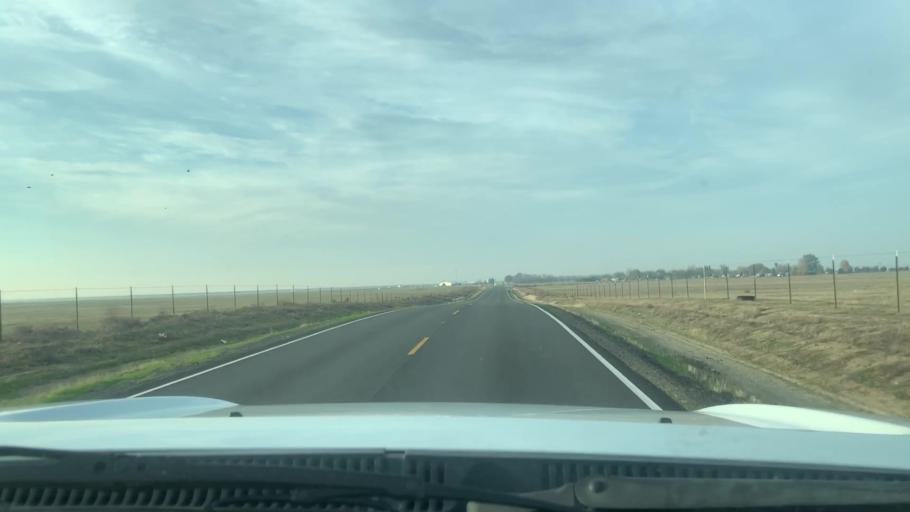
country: US
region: California
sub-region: Kern County
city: Lost Hills
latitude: 35.6041
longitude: -119.8545
